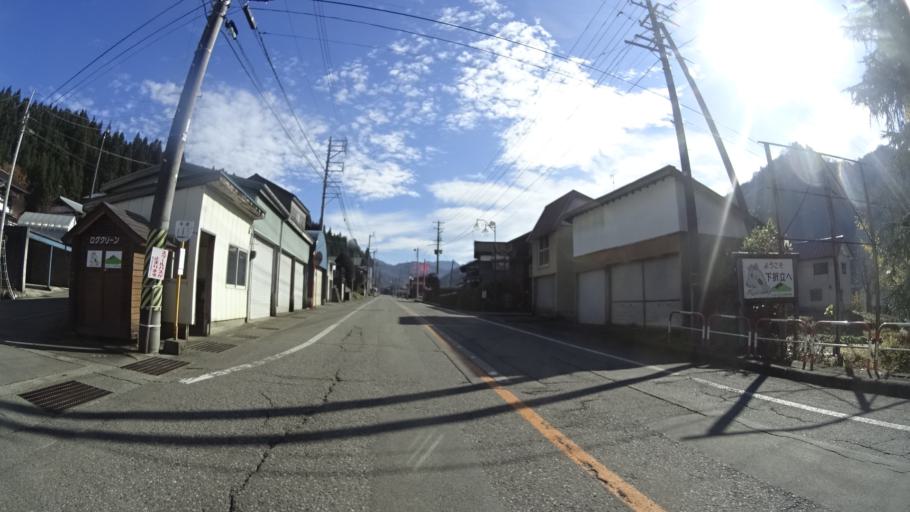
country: JP
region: Niigata
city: Muikamachi
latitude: 37.2104
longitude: 139.0573
